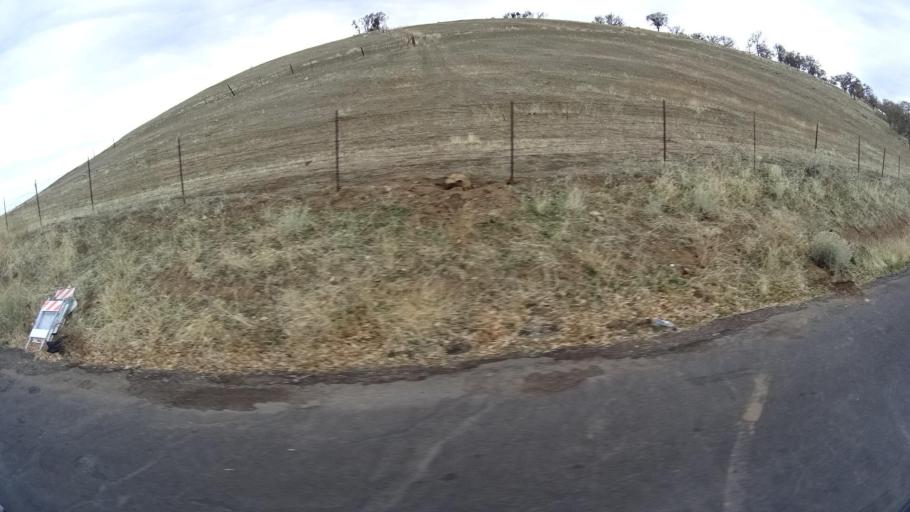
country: US
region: California
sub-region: Kern County
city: Golden Hills
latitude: 35.0940
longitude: -118.5493
